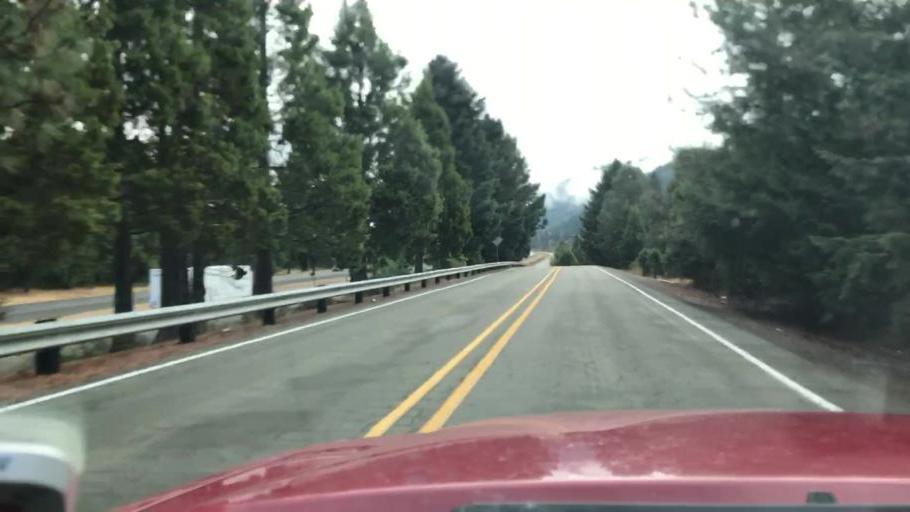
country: US
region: Oregon
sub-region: Douglas County
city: Canyonville
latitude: 42.7662
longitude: -123.3308
